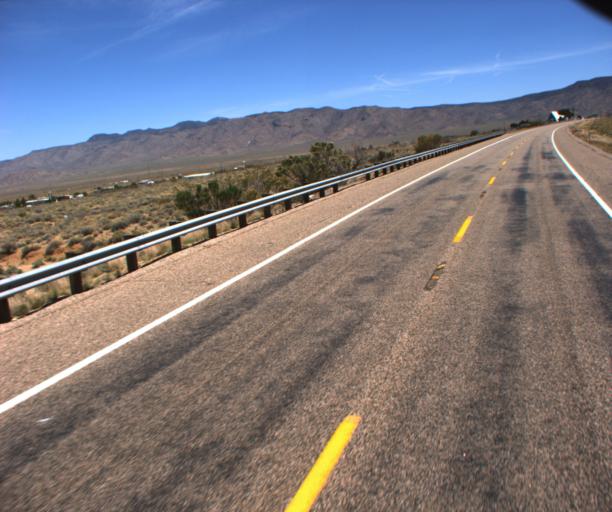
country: US
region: Arizona
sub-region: Mohave County
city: New Kingman-Butler
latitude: 35.4176
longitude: -113.8137
